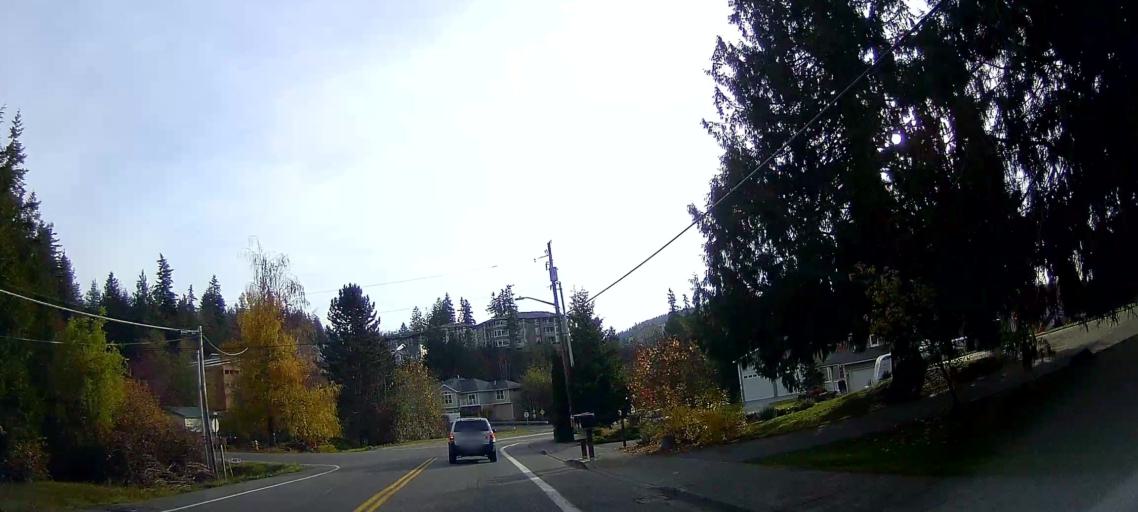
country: US
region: Washington
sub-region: Skagit County
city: Mount Vernon
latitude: 48.4146
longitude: -122.2972
